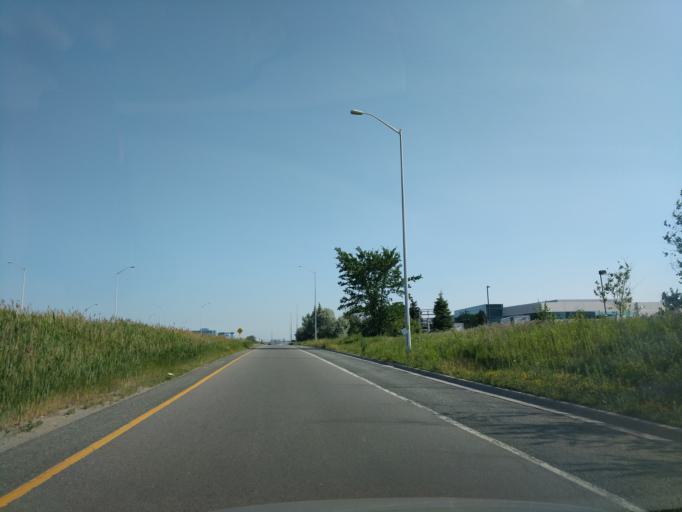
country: CA
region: Ontario
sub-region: York
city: Richmond Hill
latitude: 43.8640
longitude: -79.3756
